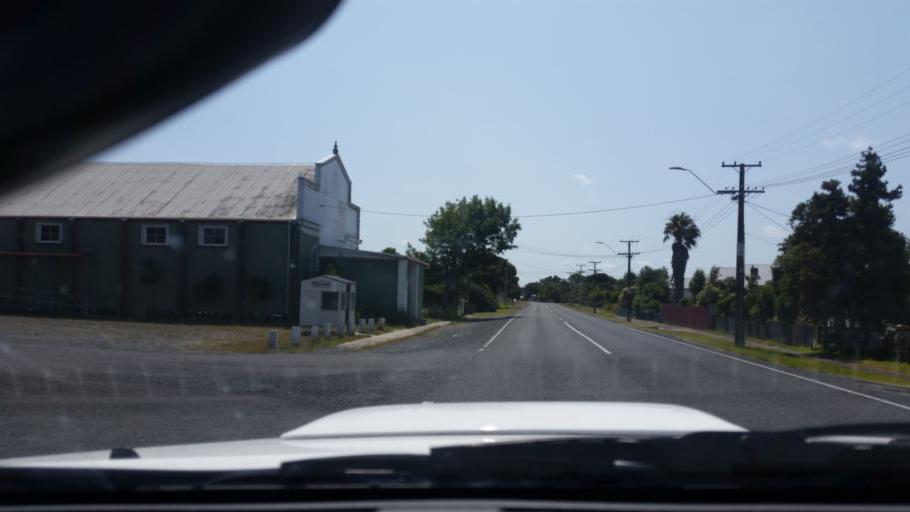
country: NZ
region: Northland
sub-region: Kaipara District
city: Dargaville
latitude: -36.0280
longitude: 173.9195
